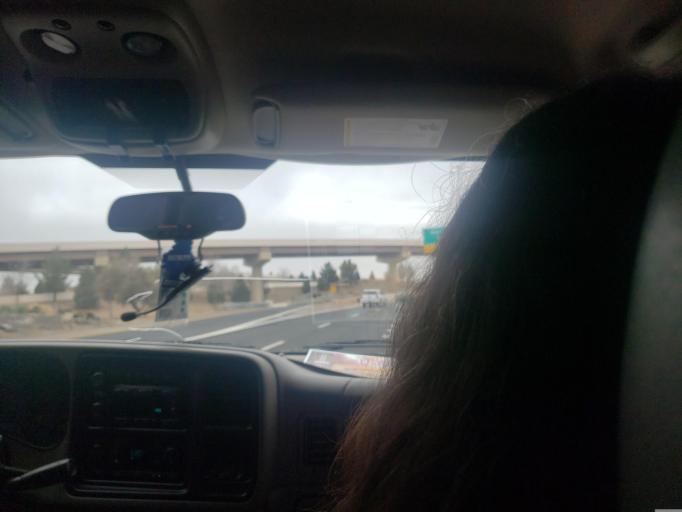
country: US
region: New Mexico
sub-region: Bernalillo County
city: Albuquerque
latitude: 35.1074
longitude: -106.7018
